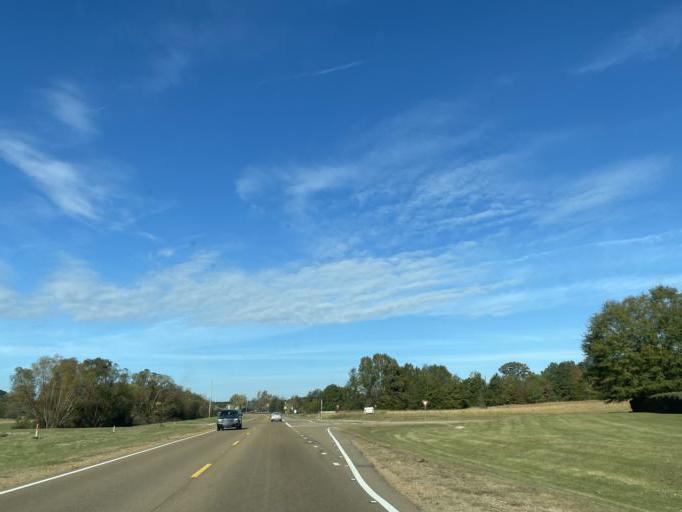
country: US
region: Mississippi
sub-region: Madison County
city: Madison
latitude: 32.4782
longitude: -90.1561
